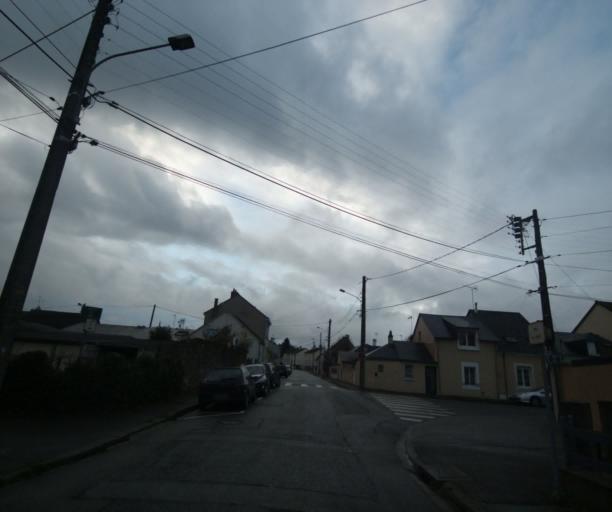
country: FR
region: Pays de la Loire
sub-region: Departement de la Sarthe
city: Coulaines
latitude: 48.0176
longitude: 0.1917
